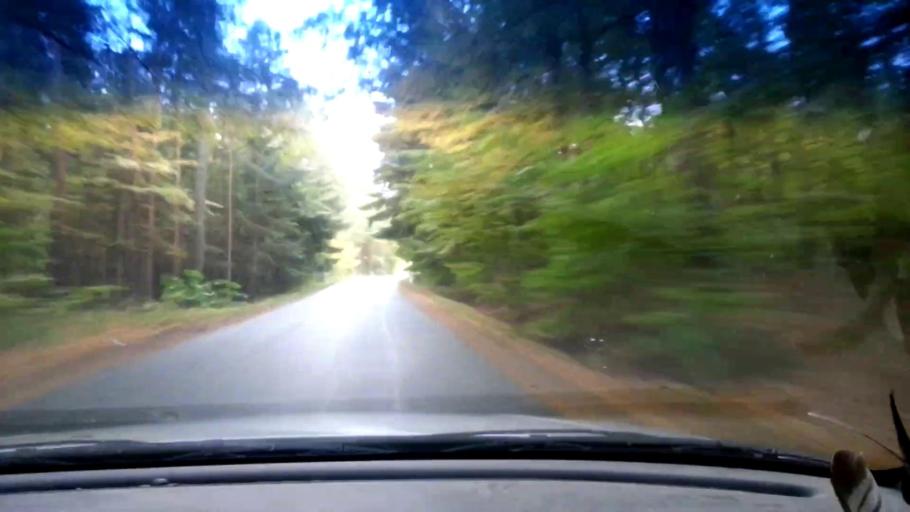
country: DE
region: Bavaria
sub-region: Upper Franconia
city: Burgebrach
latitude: 49.8007
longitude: 10.7090
